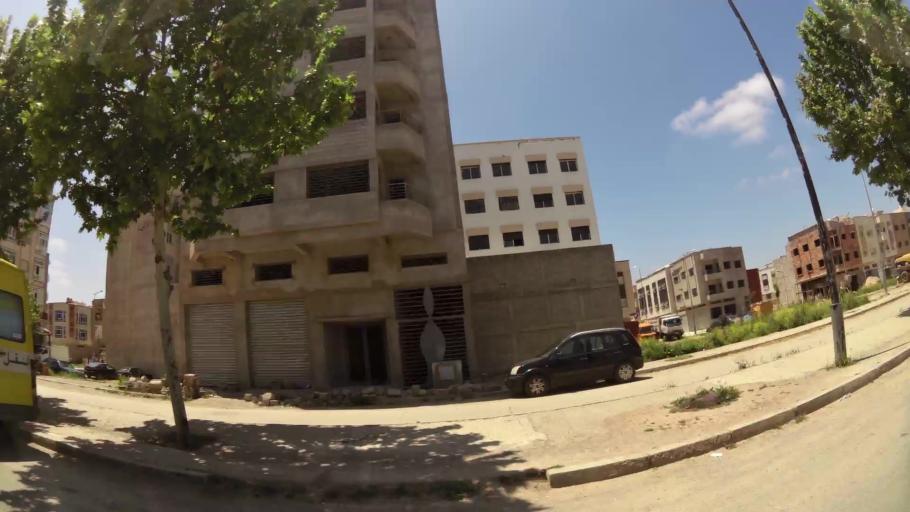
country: MA
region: Fes-Boulemane
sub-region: Fes
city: Fes
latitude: 34.0228
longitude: -5.0550
